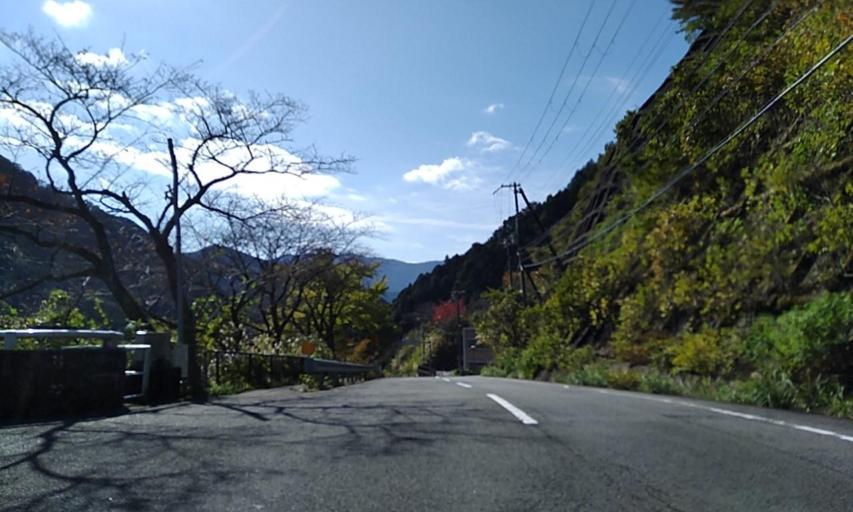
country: JP
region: Wakayama
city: Kainan
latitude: 34.0805
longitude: 135.3579
